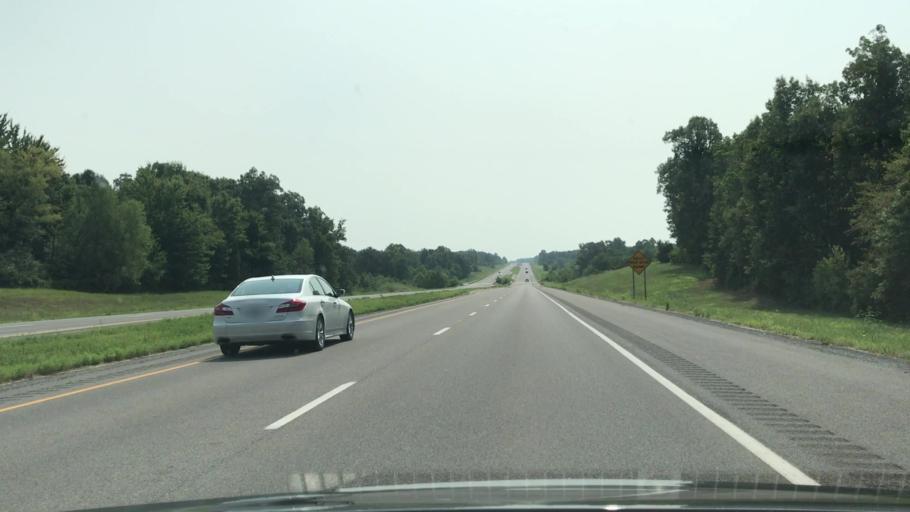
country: US
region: Kentucky
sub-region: Graves County
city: Mayfield
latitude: 36.6699
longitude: -88.5000
